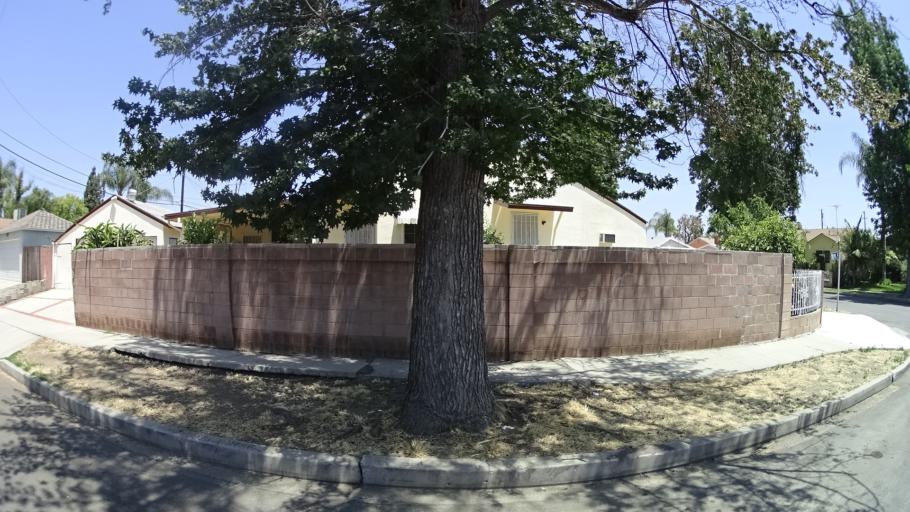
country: US
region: California
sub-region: Los Angeles County
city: Van Nuys
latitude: 34.2147
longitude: -118.4595
